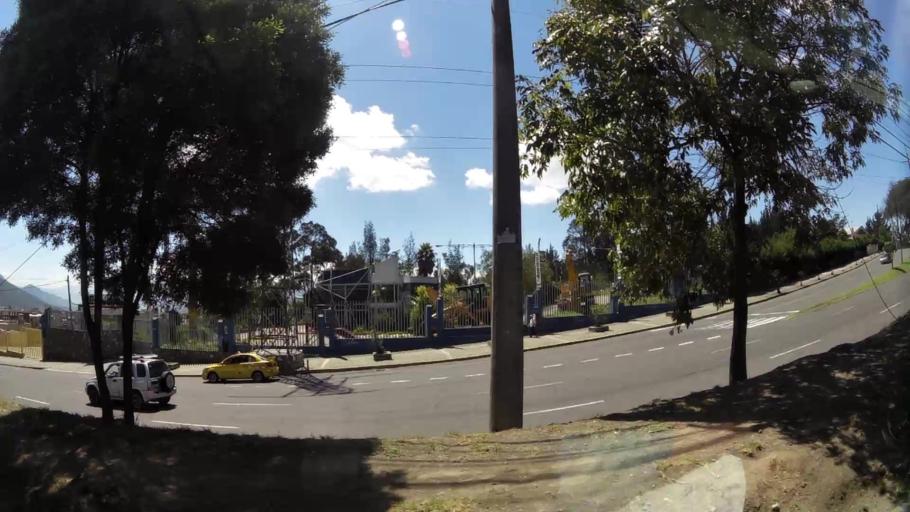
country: EC
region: Pichincha
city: Quito
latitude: -0.0944
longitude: -78.4707
